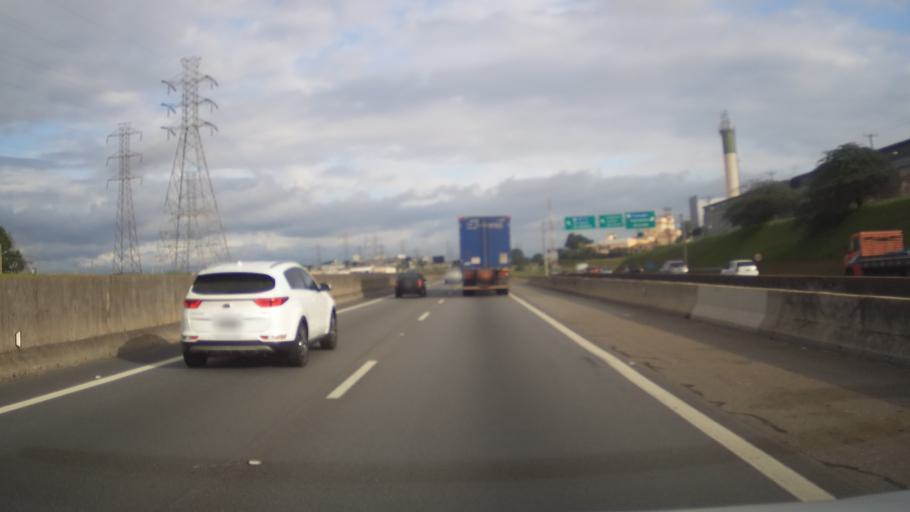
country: BR
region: Sao Paulo
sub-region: Campinas
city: Campinas
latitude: -22.9305
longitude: -47.0778
